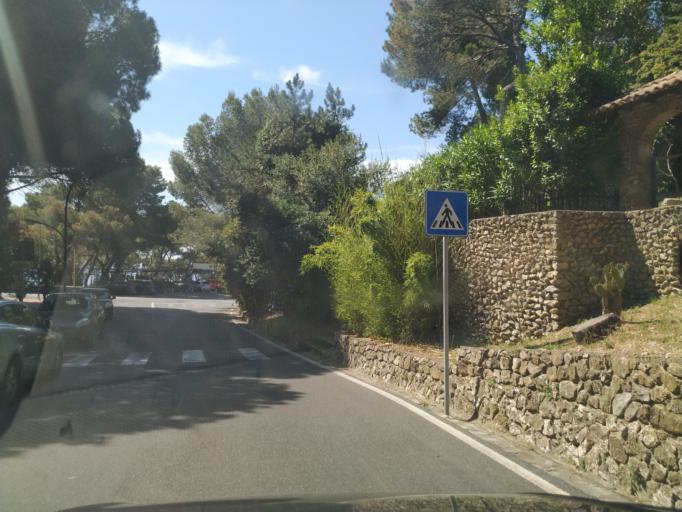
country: IT
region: Liguria
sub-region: Provincia di Savona
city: Marina di Andora
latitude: 43.9536
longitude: 8.1597
